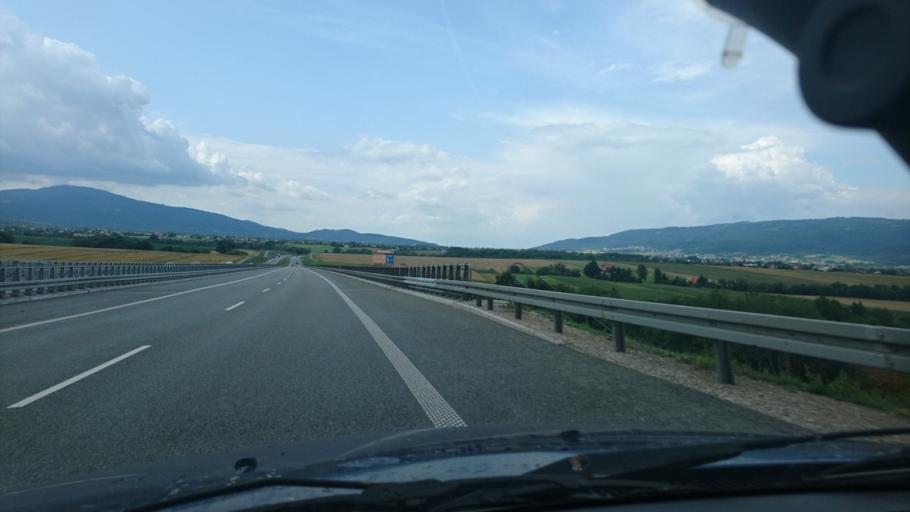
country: PL
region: Silesian Voivodeship
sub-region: Powiat zywiecki
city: Pietrzykowice
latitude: 49.6976
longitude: 19.1330
